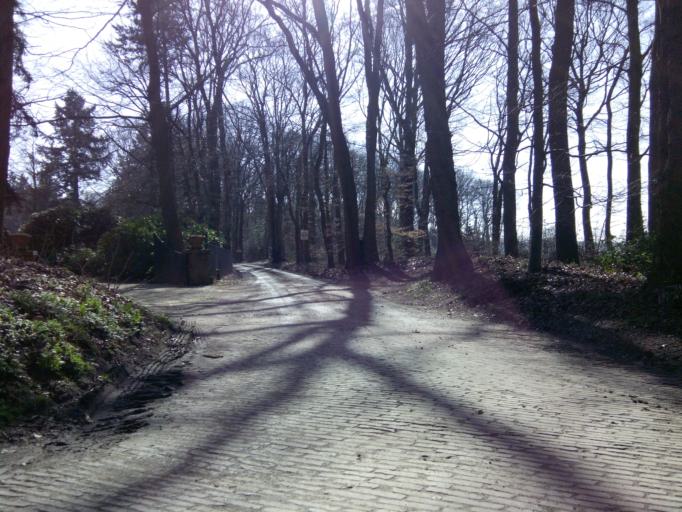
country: NL
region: Gelderland
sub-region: Gemeente Barneveld
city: Garderen
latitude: 52.2188
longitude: 5.7309
